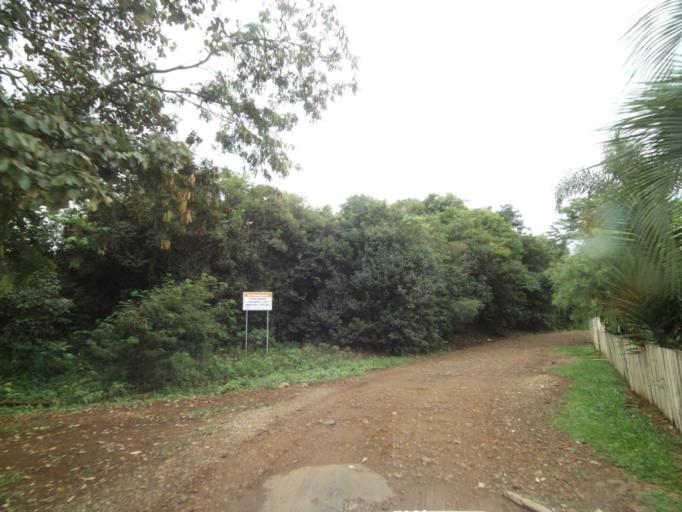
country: BR
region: Parana
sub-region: Guaraniacu
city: Guaraniacu
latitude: -25.1127
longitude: -52.8493
